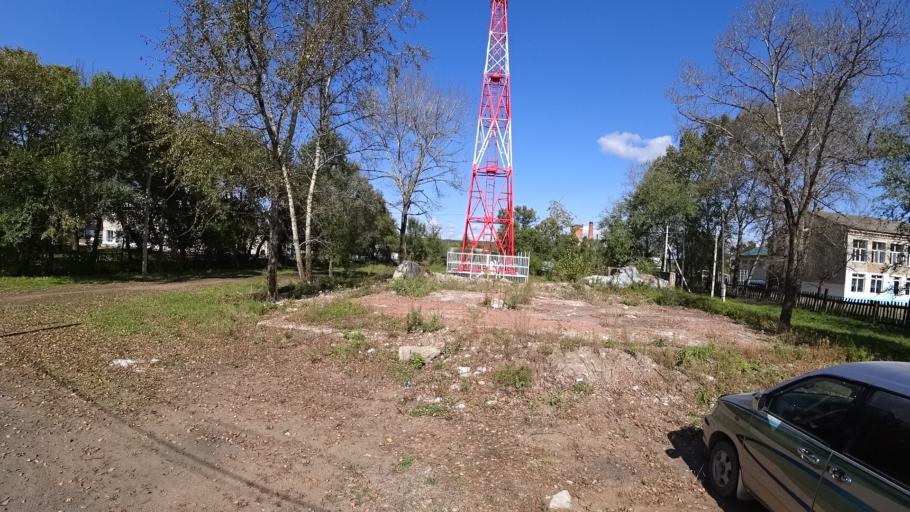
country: RU
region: Amur
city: Arkhara
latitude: 49.4031
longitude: 130.1393
